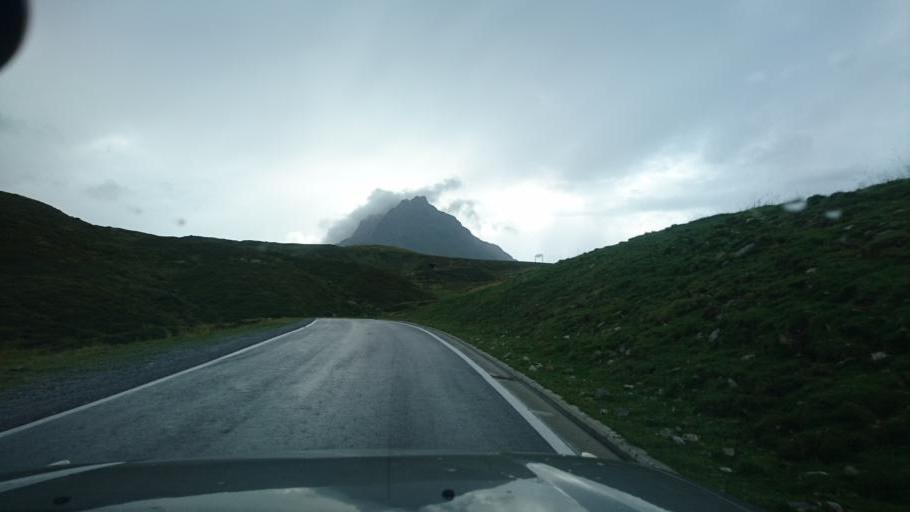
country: AT
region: Tyrol
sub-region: Politischer Bezirk Landeck
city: Galtur
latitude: 46.9187
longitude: 10.1085
